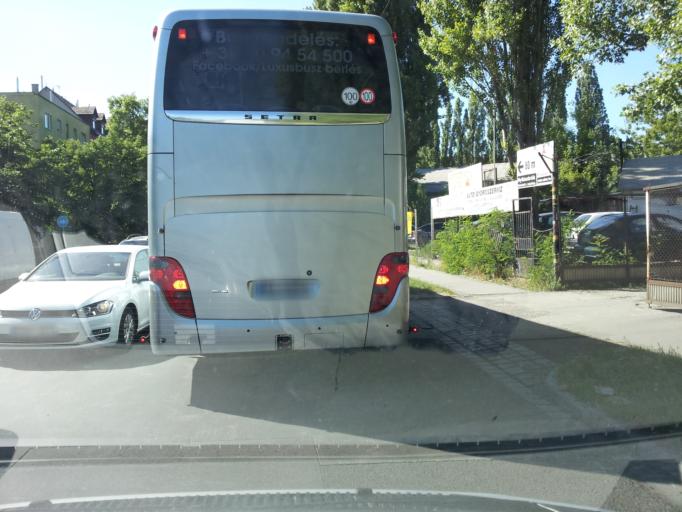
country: HU
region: Budapest
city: Budapest XIII. keruelet
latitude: 47.5260
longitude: 19.0876
